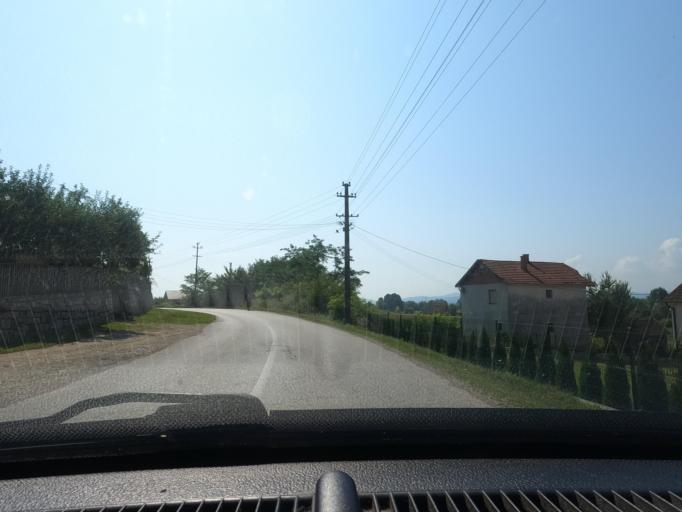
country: RS
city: Jadranska Lesnica
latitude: 44.5487
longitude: 19.3419
